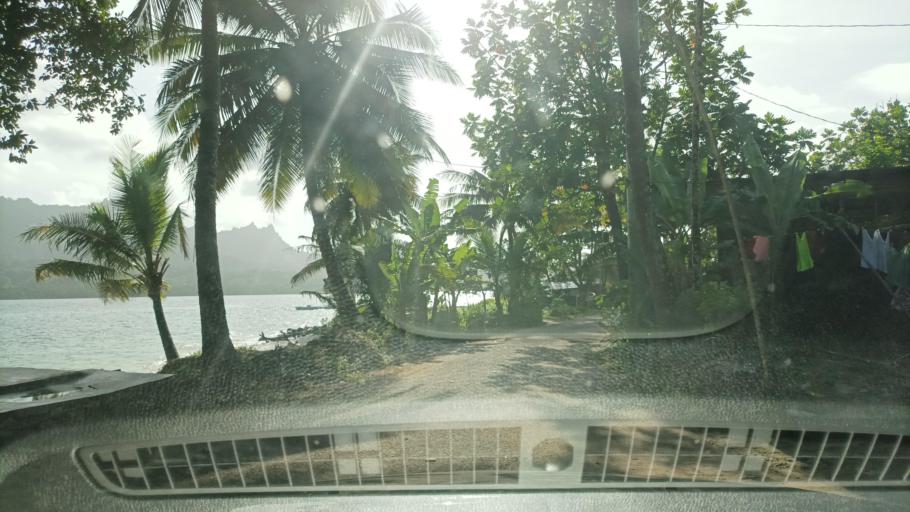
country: FM
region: Kosrae
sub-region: Lelu Municipality
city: Lelu
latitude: 5.3276
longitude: 163.0298
